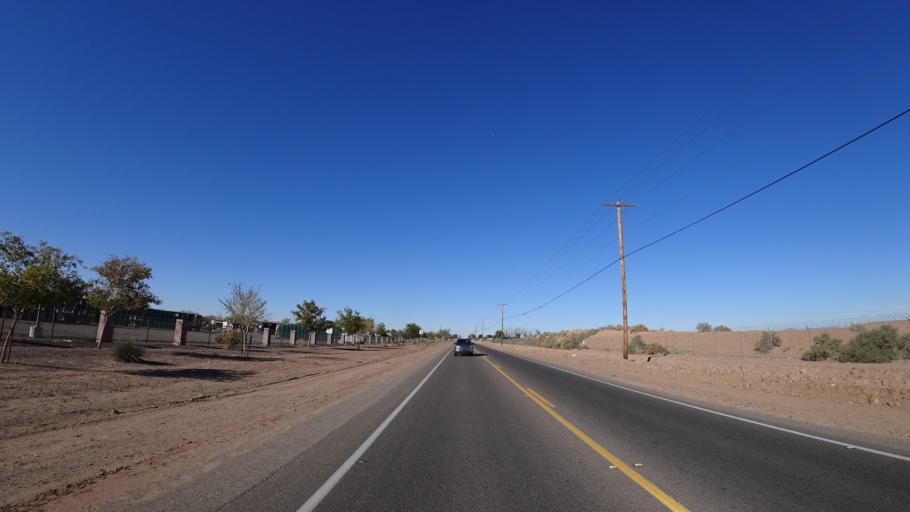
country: US
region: Arizona
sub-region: Maricopa County
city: Laveen
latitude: 33.4016
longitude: -112.2042
